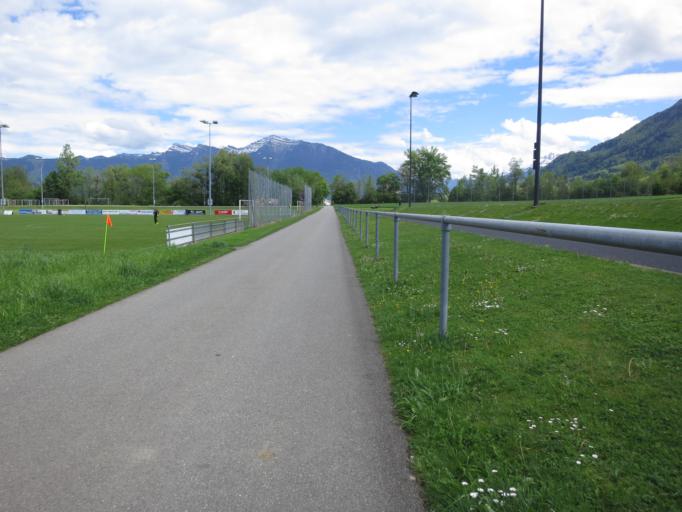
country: CH
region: Schwyz
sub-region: Bezirk March
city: Reichenburg
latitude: 47.1749
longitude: 8.9592
